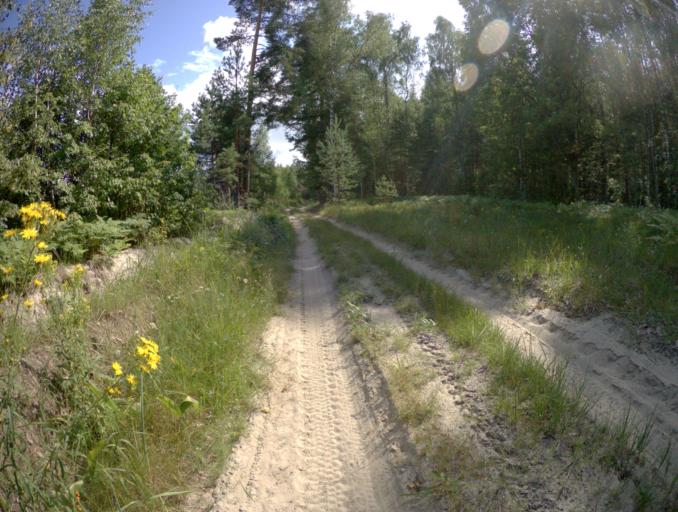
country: RU
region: Vladimir
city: Vorsha
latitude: 55.9273
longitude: 40.1455
